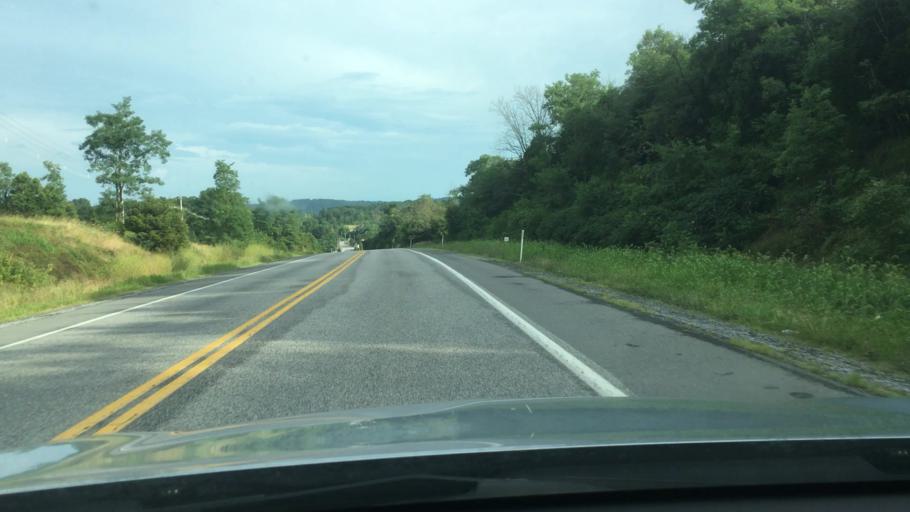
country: US
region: Pennsylvania
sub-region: York County
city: Dover
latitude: 40.0710
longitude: -76.9232
